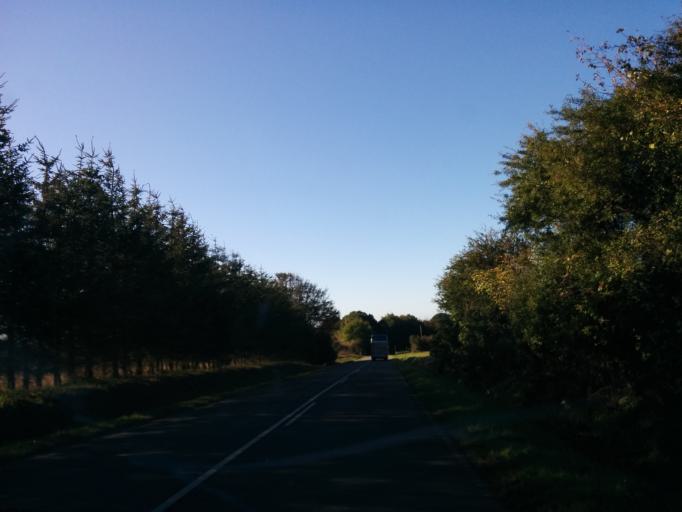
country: DK
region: South Denmark
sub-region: Kolding Kommune
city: Sonder Bjert
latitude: 55.4135
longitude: 9.5603
